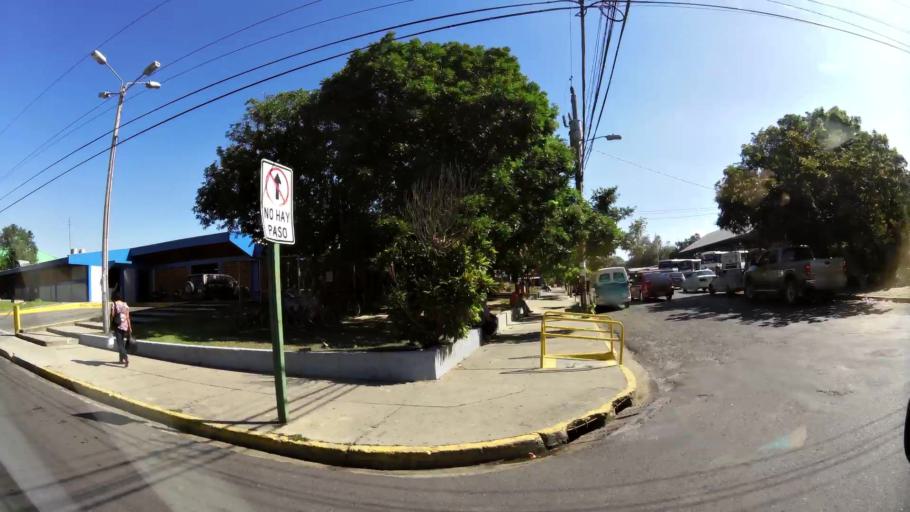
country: CR
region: Guanacaste
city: Liberia
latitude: 10.6312
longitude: -85.4442
